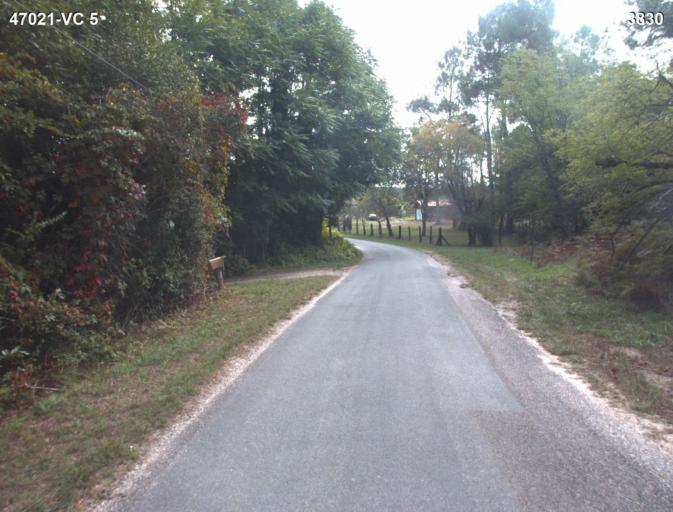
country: FR
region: Aquitaine
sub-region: Departement du Lot-et-Garonne
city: Barbaste
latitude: 44.1436
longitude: 0.2518
